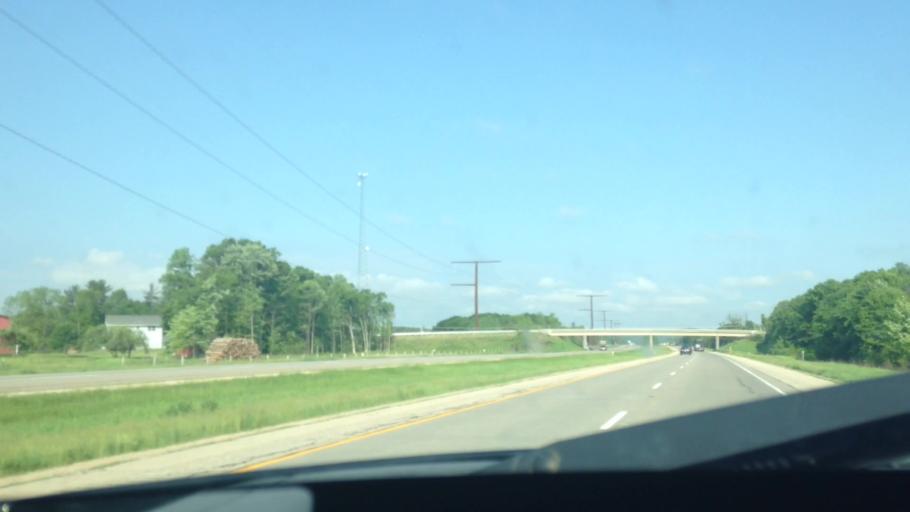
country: US
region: Wisconsin
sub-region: Juneau County
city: New Lisbon
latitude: 43.9047
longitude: -90.2076
